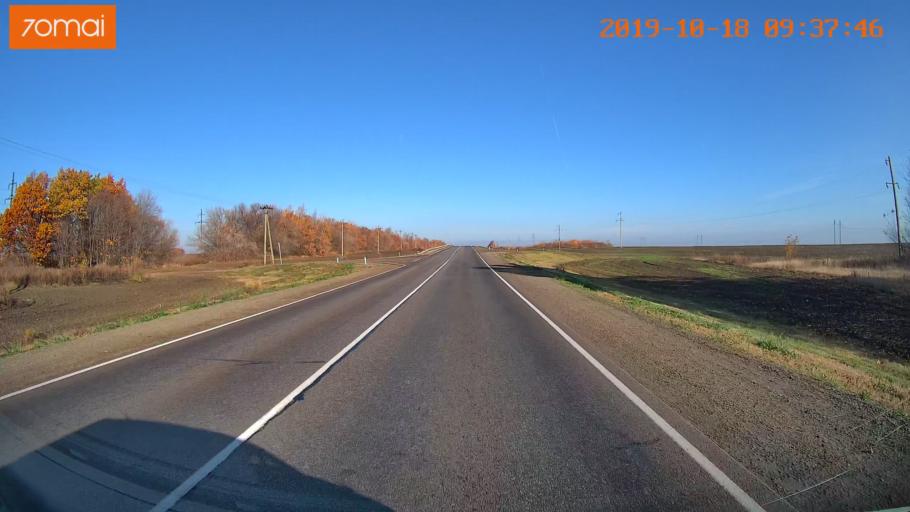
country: RU
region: Tula
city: Yefremov
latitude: 53.2275
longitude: 38.1397
